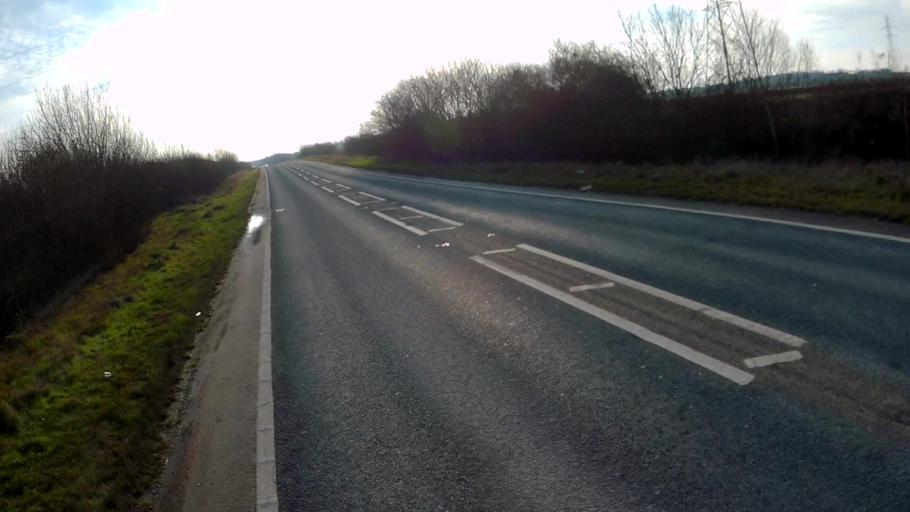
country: GB
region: England
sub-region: Lincolnshire
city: Bourne
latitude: 52.7642
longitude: -0.3958
